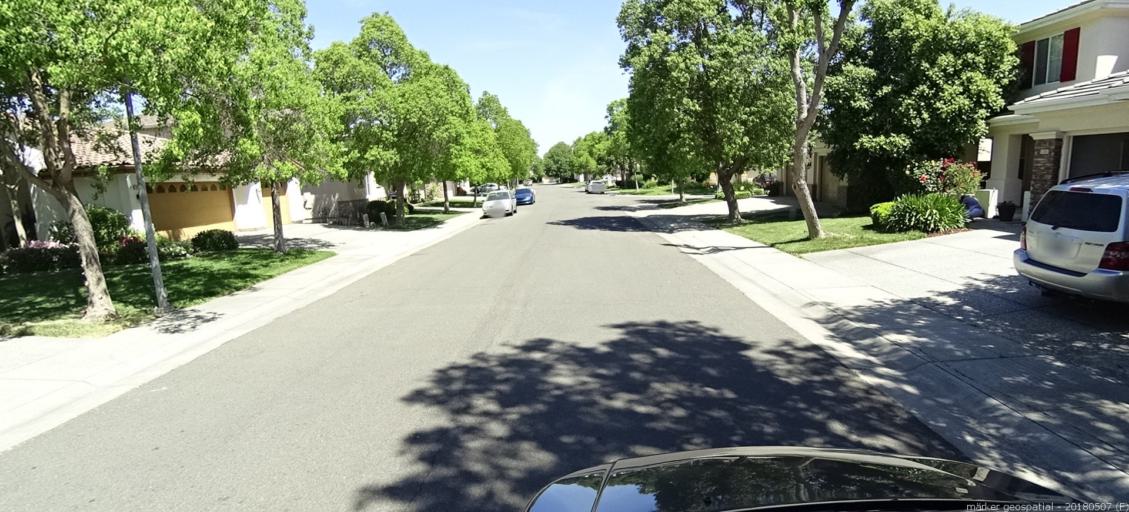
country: US
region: California
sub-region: Sacramento County
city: Rio Linda
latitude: 38.6671
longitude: -121.5091
